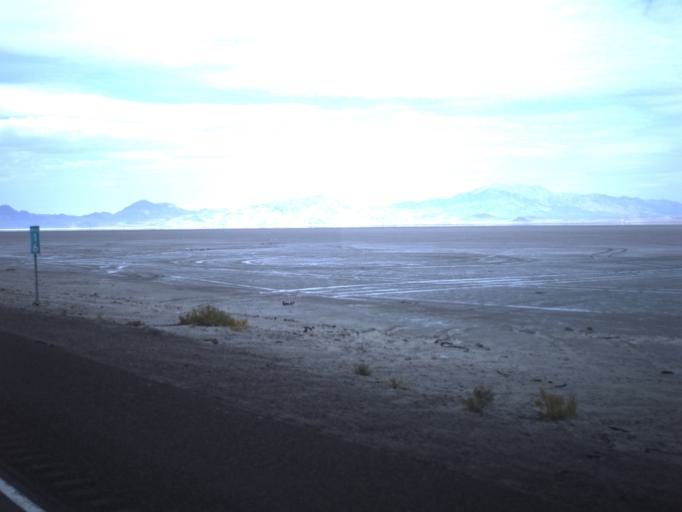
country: US
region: Utah
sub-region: Tooele County
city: Wendover
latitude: 40.7371
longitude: -113.7409
